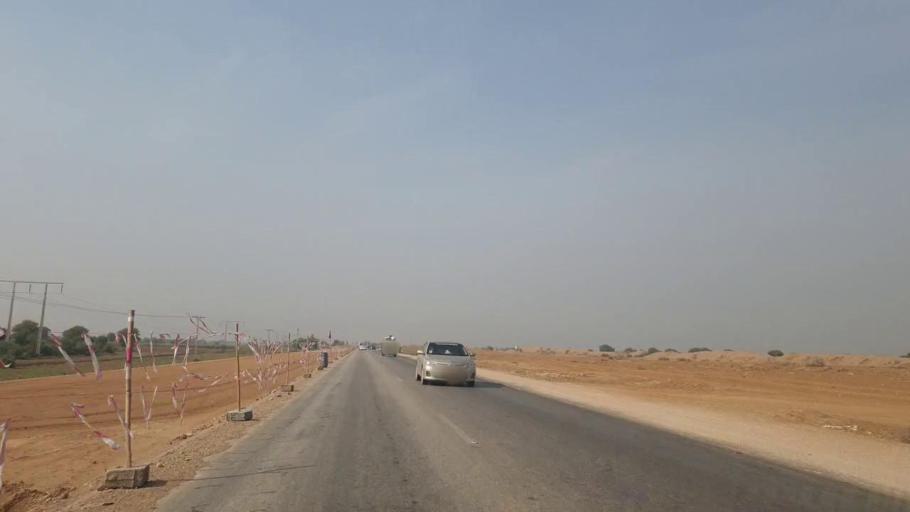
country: PK
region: Sindh
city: Sann
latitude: 26.1260
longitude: 68.0541
